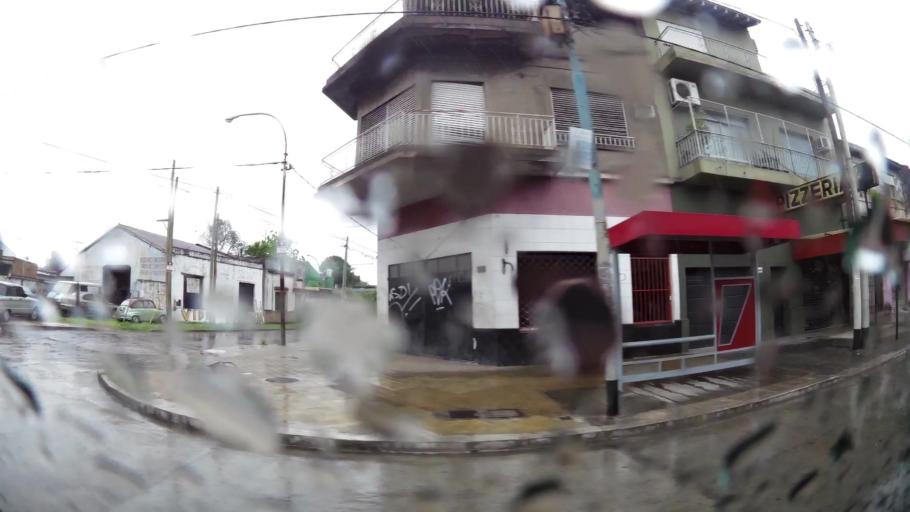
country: AR
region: Buenos Aires
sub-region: Partido de Lanus
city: Lanus
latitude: -34.7021
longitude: -58.4136
